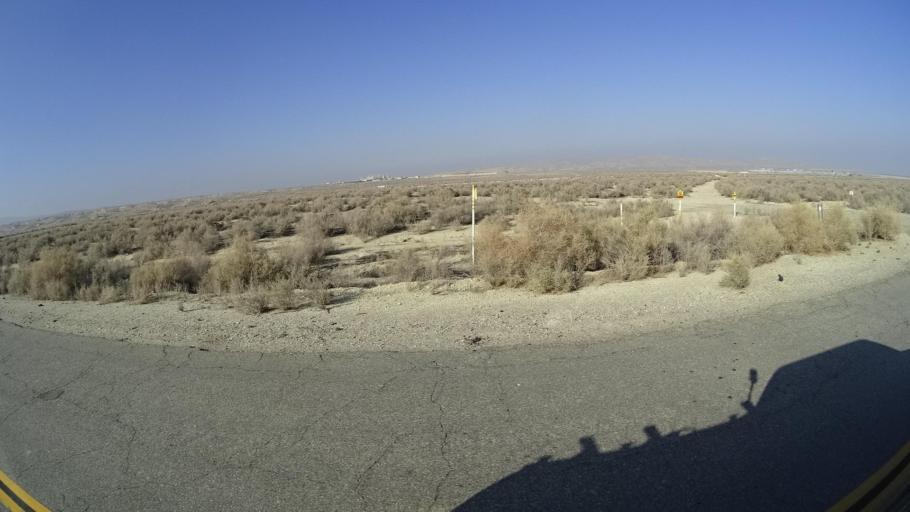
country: US
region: California
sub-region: Kern County
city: Maricopa
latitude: 35.1009
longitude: -119.3951
